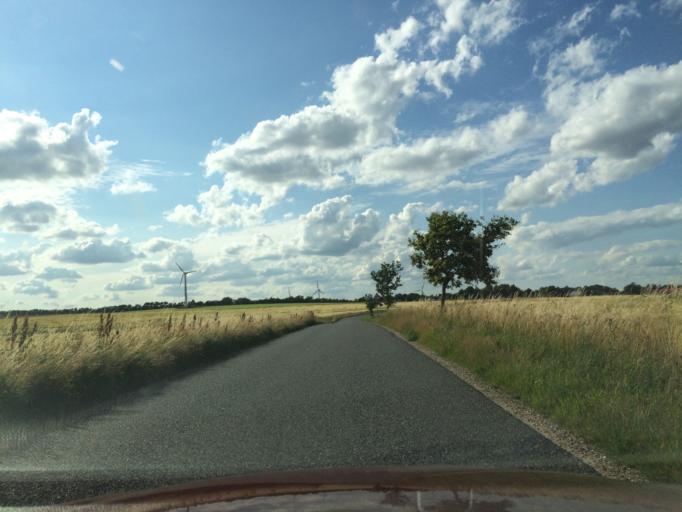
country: DK
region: Central Jutland
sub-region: Silkeborg Kommune
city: Svejbaek
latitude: 56.2474
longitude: 9.7157
